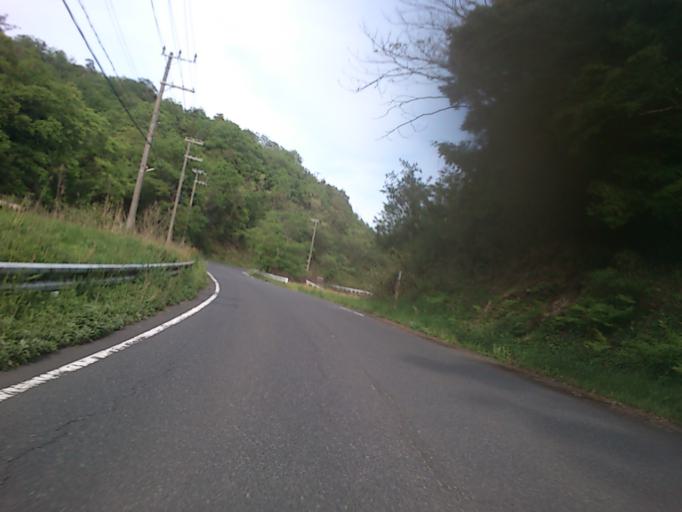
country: JP
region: Kyoto
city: Miyazu
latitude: 35.5740
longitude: 135.1075
